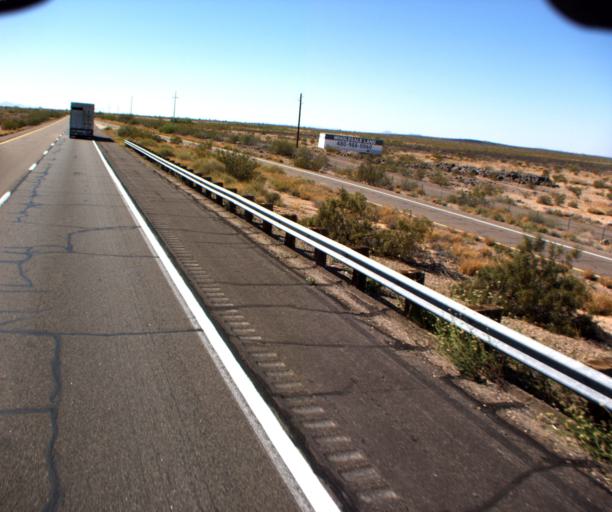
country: US
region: Arizona
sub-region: Maricopa County
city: Gila Bend
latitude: 32.8584
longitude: -113.2156
